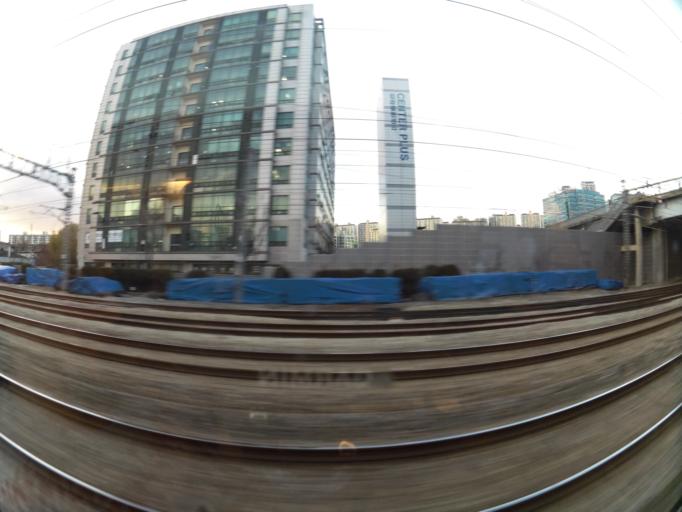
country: KR
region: Gyeonggi-do
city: Kwangmyong
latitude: 37.5115
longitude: 126.8974
